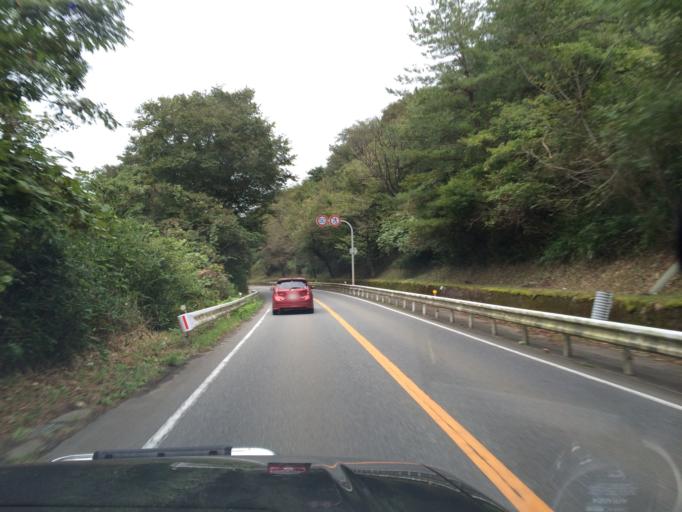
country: JP
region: Hyogo
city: Toyooka
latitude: 35.4104
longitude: 134.7818
